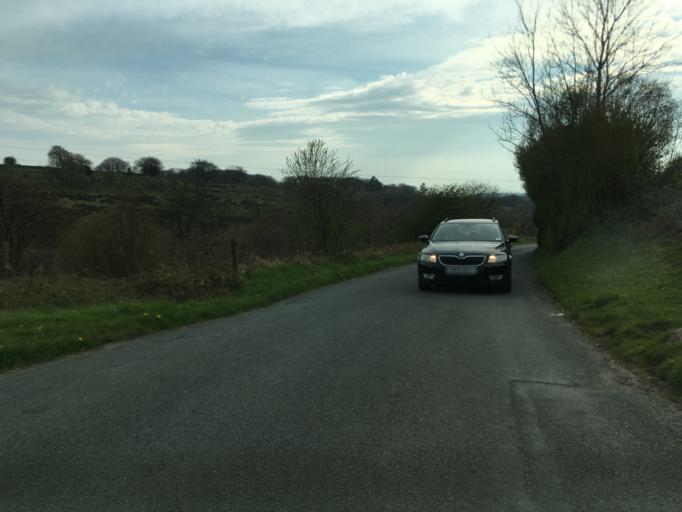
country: GB
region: Wales
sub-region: Caerphilly County Borough
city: Caerphilly
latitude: 51.5597
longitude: -3.2269
